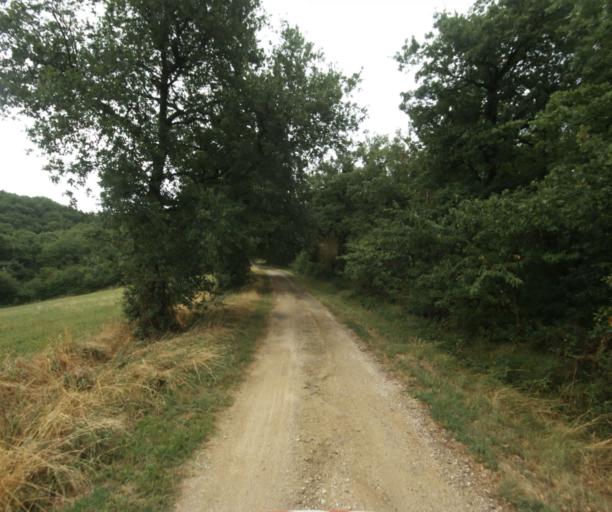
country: FR
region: Midi-Pyrenees
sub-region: Departement de la Haute-Garonne
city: Revel
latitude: 43.4143
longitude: 1.9819
